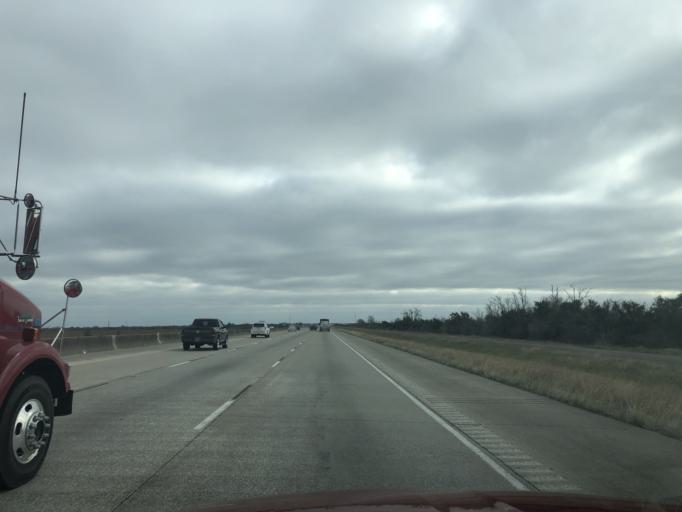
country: US
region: Texas
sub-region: Chambers County
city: Winnie
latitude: 29.8286
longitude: -94.4650
